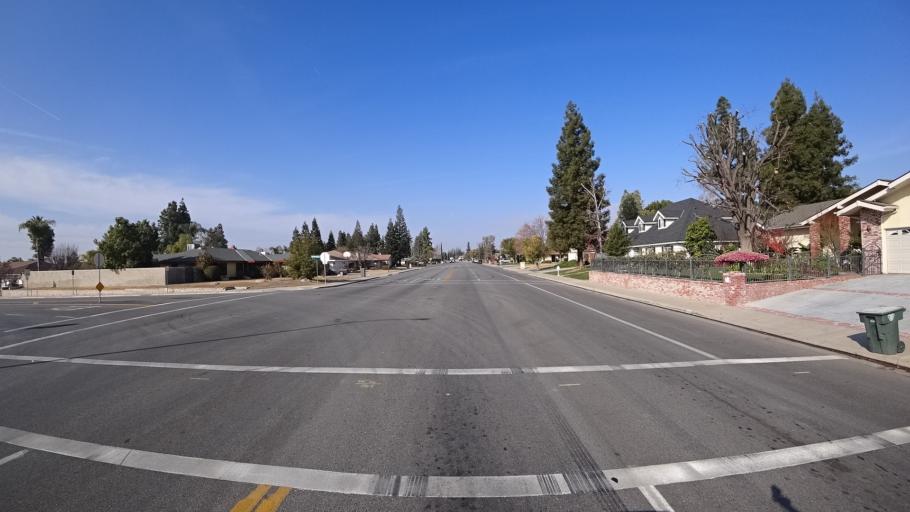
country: US
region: California
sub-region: Kern County
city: Oildale
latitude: 35.4056
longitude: -118.9378
